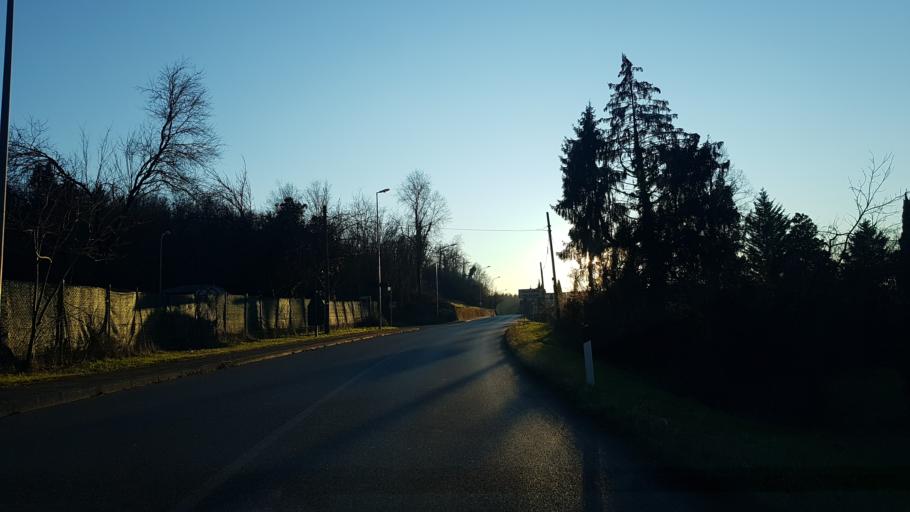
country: IT
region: Friuli Venezia Giulia
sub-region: Provincia di Udine
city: Tricesimo
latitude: 46.1666
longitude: 13.2141
